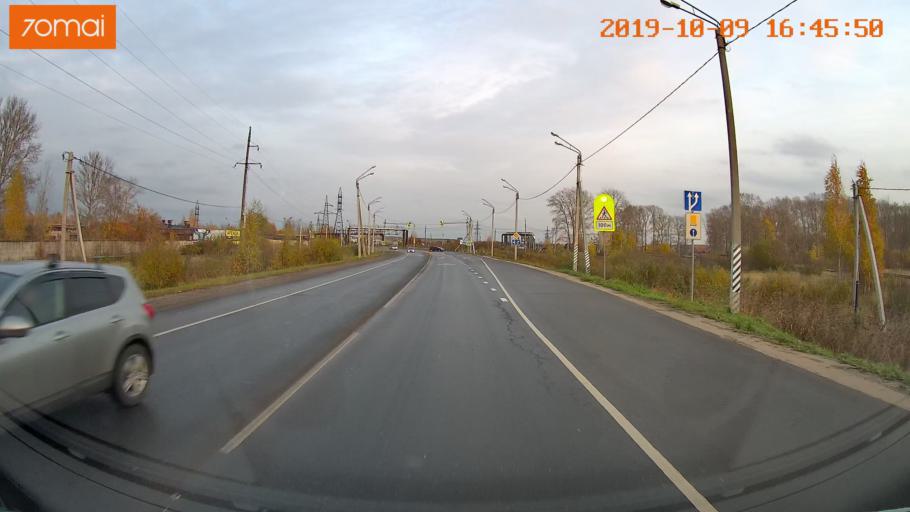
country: RU
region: Kostroma
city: Volgorechensk
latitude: 57.4448
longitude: 41.1607
